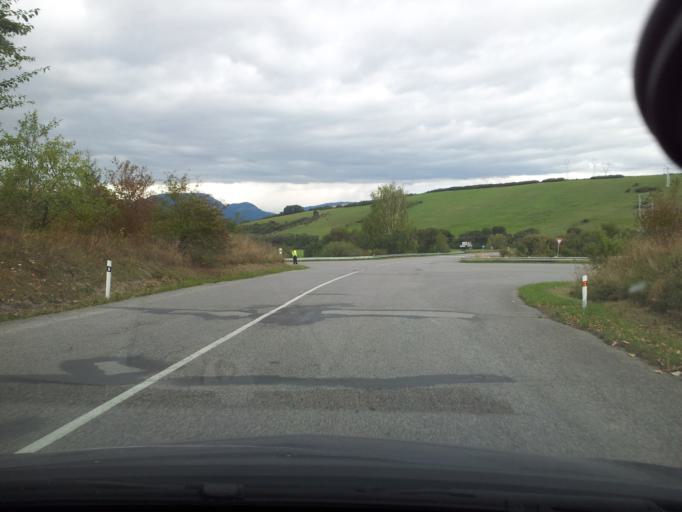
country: SK
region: Zilinsky
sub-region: Okres Liptovsky Mikulas
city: Liptovsky Mikulas
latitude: 49.0587
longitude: 19.4755
